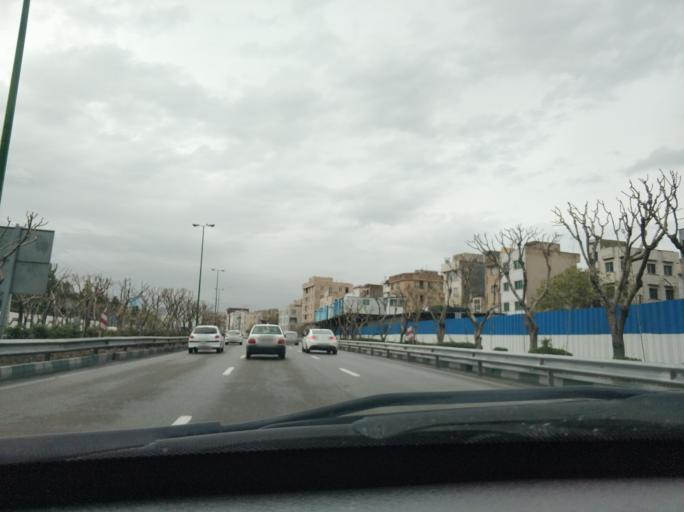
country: IR
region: Tehran
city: Tehran
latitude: 35.7096
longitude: 51.4430
